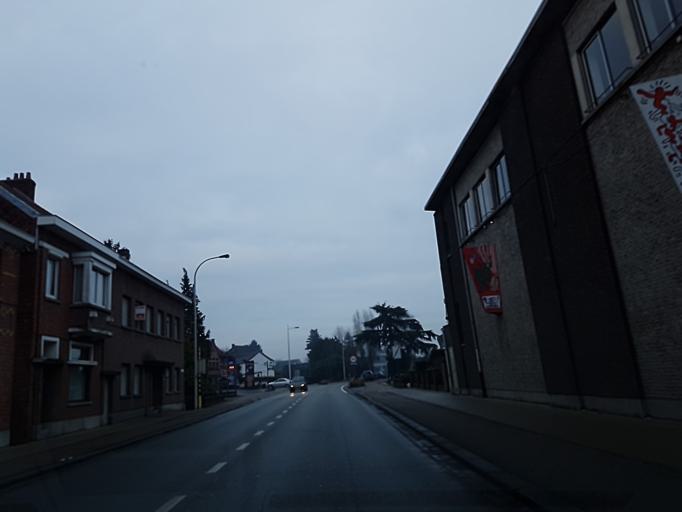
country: BE
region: Flanders
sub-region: Provincie Antwerpen
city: Nijlen
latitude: 51.1621
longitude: 4.6739
